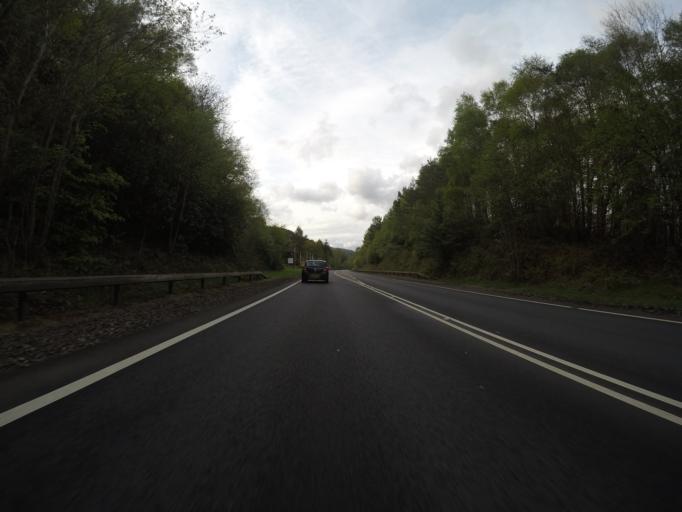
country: GB
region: Scotland
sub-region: Argyll and Bute
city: Helensburgh
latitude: 56.1434
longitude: -4.6634
